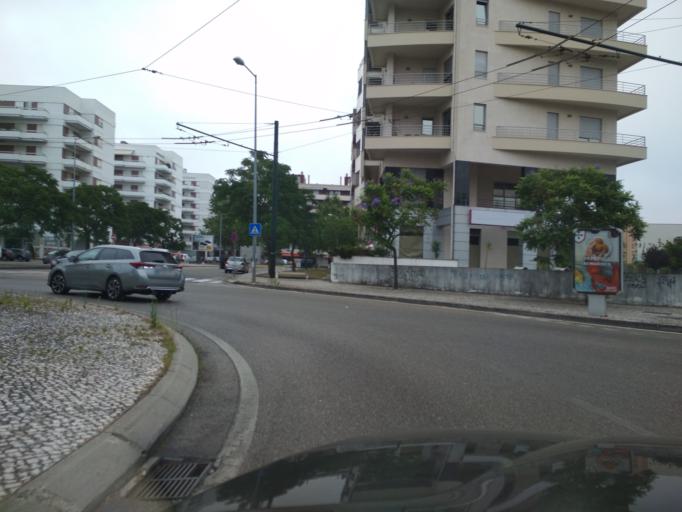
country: PT
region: Coimbra
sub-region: Coimbra
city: Coimbra
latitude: 40.2025
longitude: -8.4042
